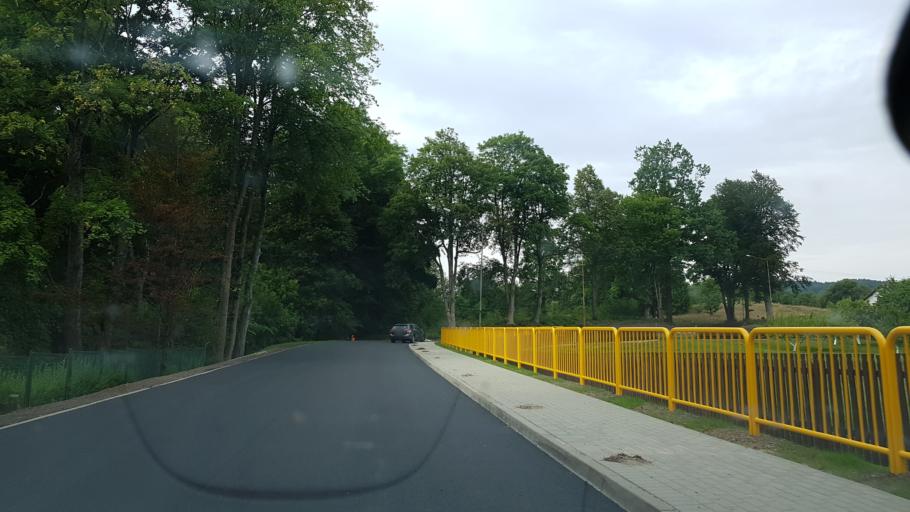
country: PL
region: Lower Silesian Voivodeship
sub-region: Powiat jeleniogorski
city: Janowice Wielkie
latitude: 50.8819
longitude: 15.9249
